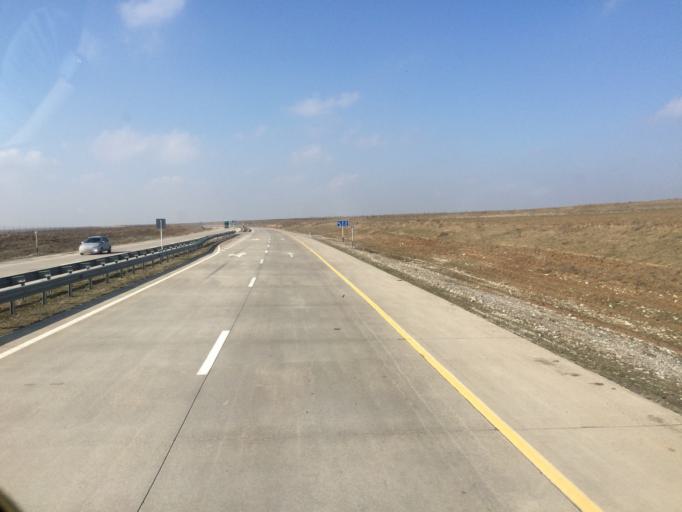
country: KZ
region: Ongtustik Qazaqstan
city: Shymkent
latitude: 42.4896
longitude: 69.5151
